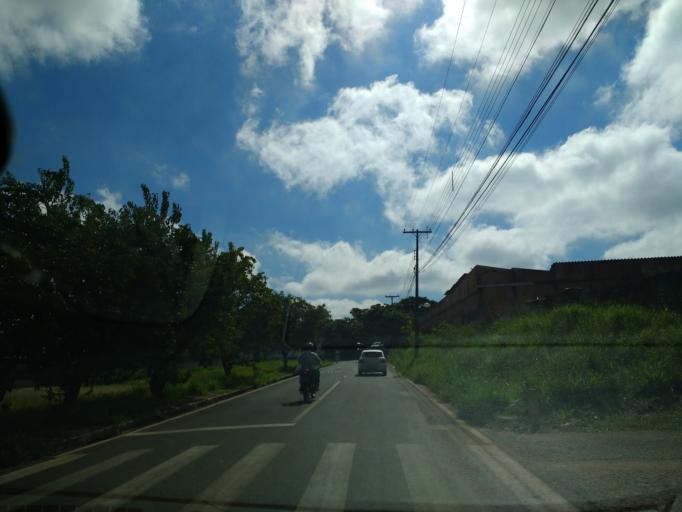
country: BR
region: Parana
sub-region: Umuarama
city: Umuarama
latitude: -23.7748
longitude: -53.3006
